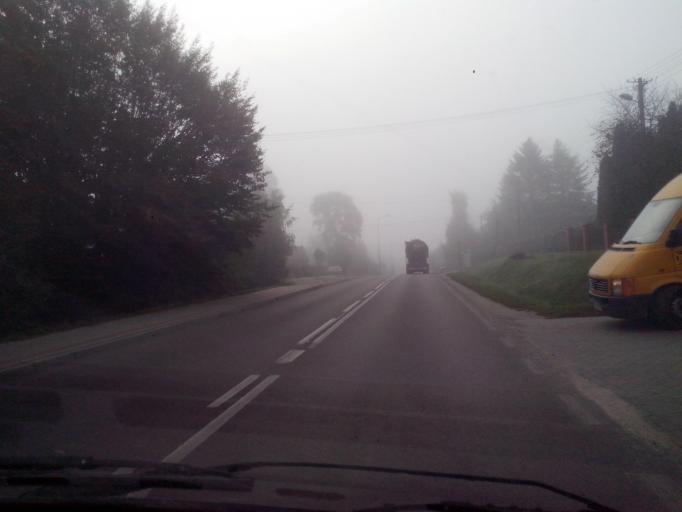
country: PL
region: Subcarpathian Voivodeship
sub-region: Przemysl
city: Przemysl
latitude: 49.7915
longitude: 22.7239
